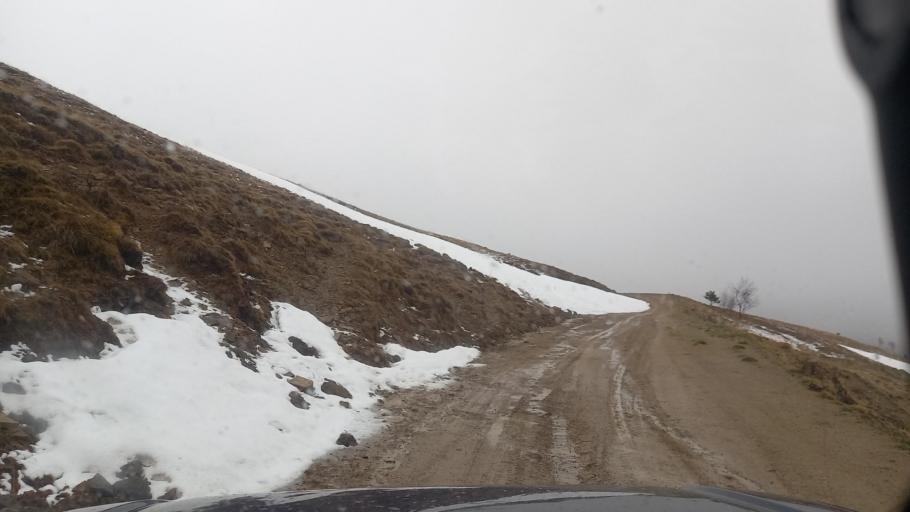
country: RU
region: Karachayevo-Cherkesiya
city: Uchkeken
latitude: 43.6037
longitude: 42.5635
